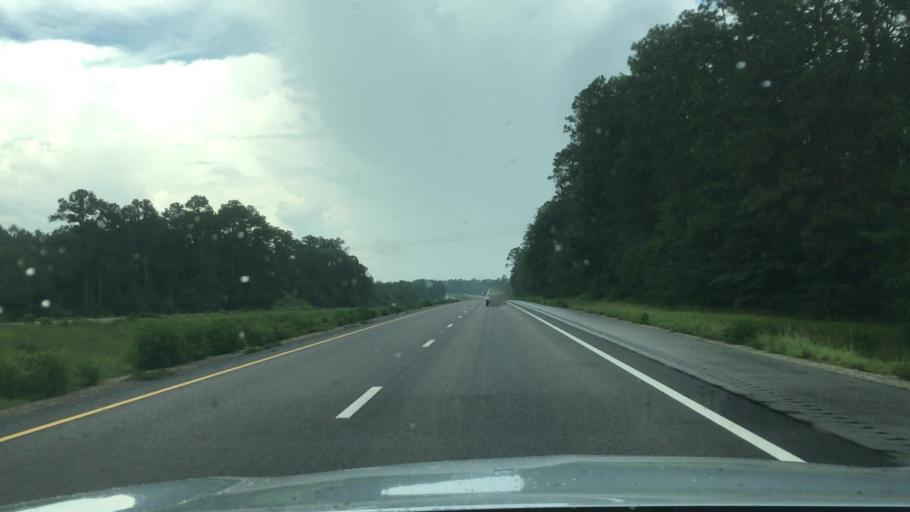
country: US
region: Mississippi
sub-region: Lamar County
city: Purvis
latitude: 31.2152
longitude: -89.3296
